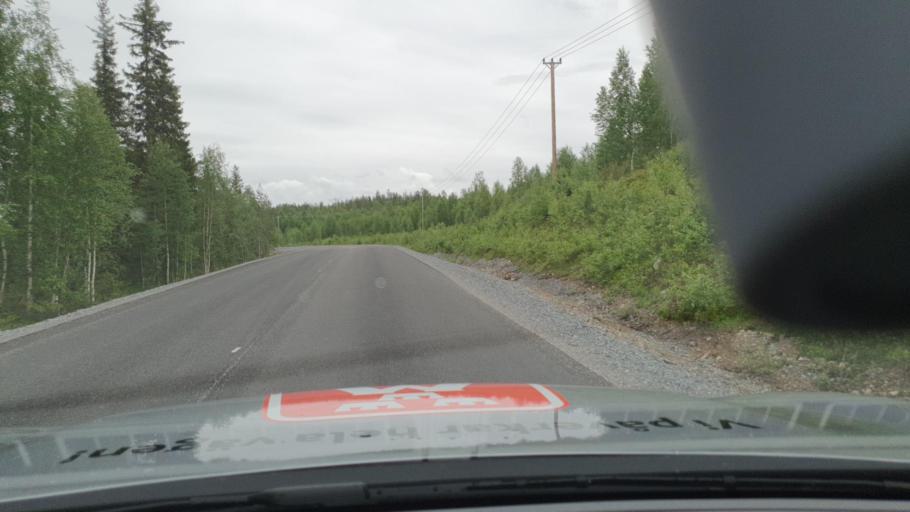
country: SE
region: Norrbotten
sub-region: Overtornea Kommun
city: OEvertornea
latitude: 66.6272
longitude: 23.2720
